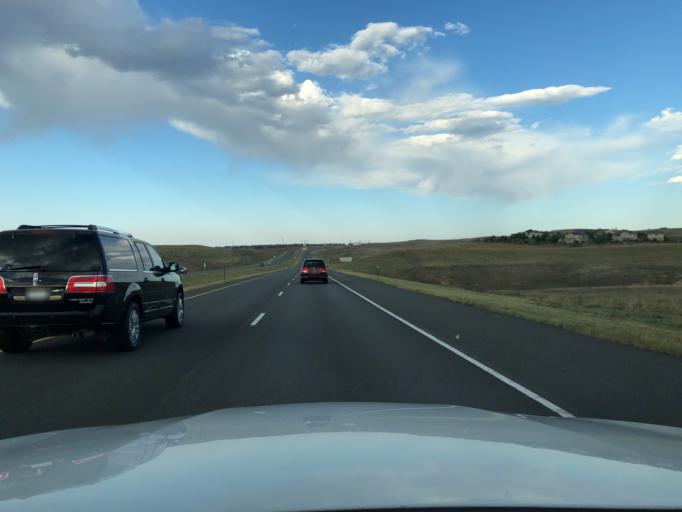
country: US
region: Colorado
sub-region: Boulder County
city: Lafayette
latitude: 39.9732
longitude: -105.0621
